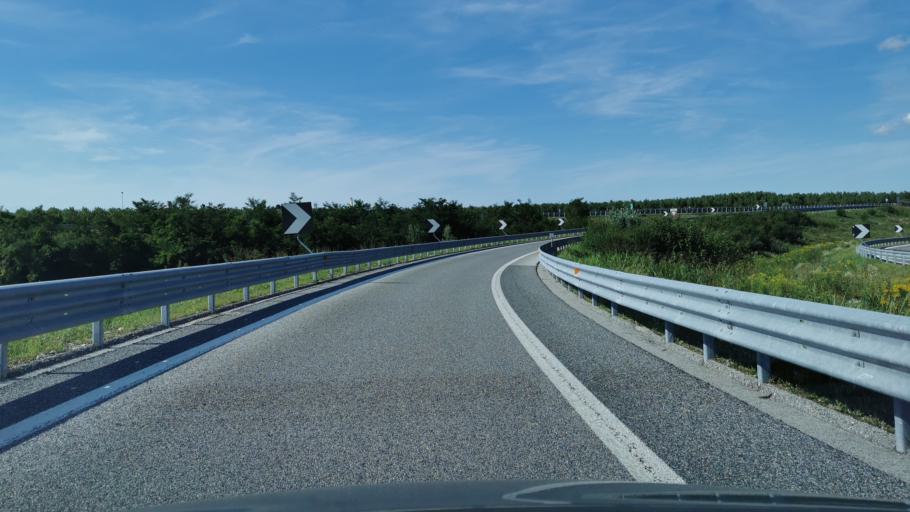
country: IT
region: Piedmont
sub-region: Provincia di Cuneo
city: Cuneo
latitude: 44.4223
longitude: 7.5901
